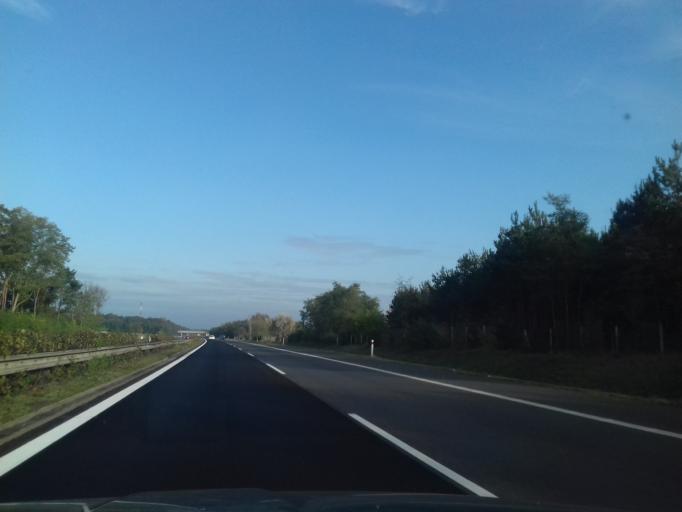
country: SK
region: Bratislavsky
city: Stupava
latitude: 48.3398
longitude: 17.0237
